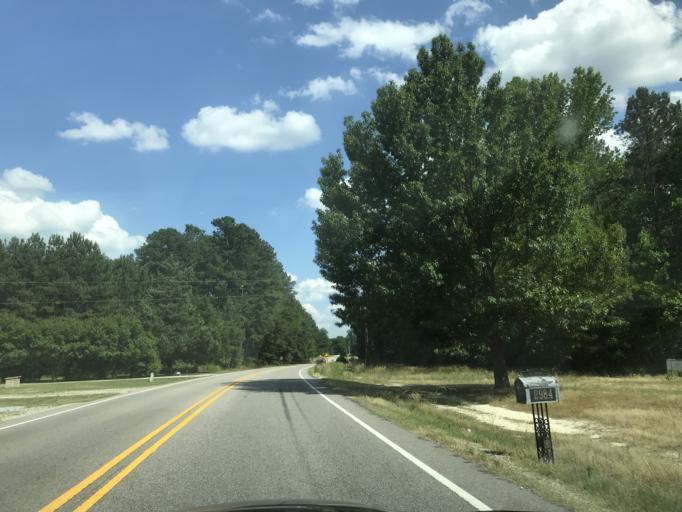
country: US
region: North Carolina
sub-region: Wake County
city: Rolesville
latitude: 35.9756
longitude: -78.3472
